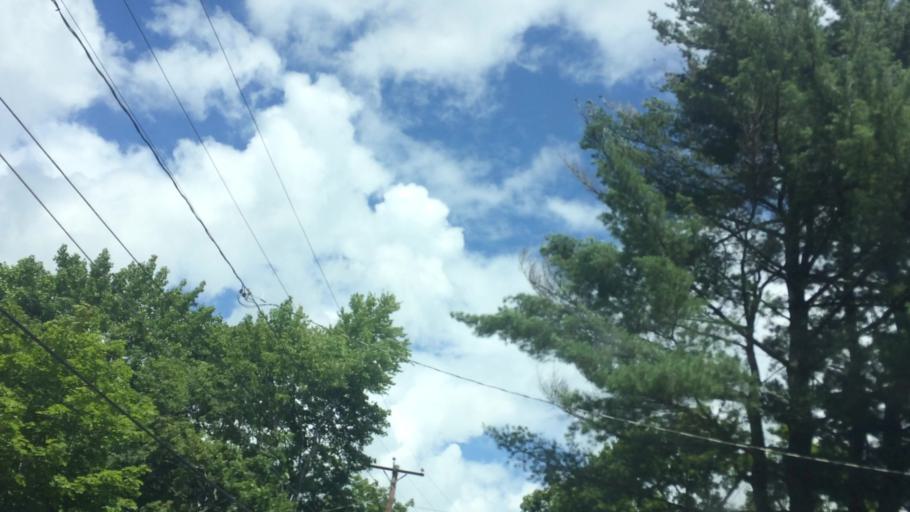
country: US
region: Massachusetts
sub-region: Middlesex County
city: Maynard
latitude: 42.4216
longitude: -71.4449
